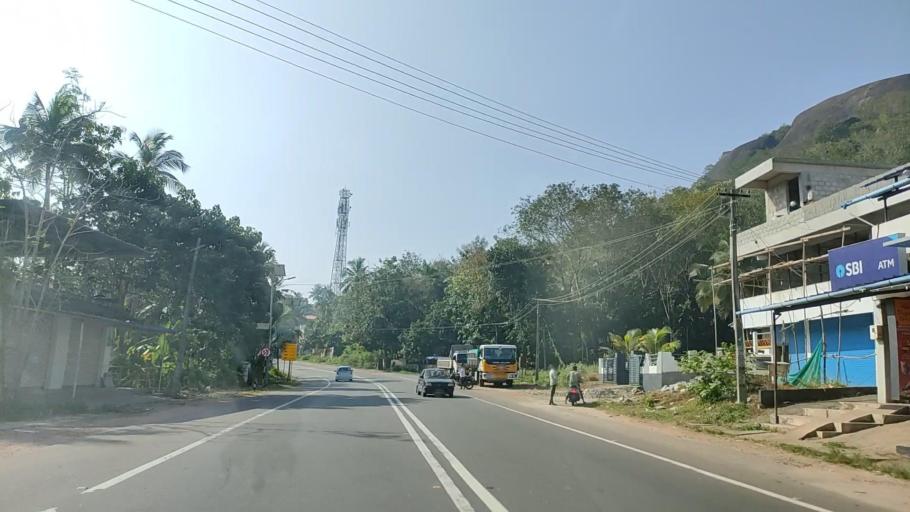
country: IN
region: Kerala
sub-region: Kollam
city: Punalur
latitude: 8.8677
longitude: 76.8701
